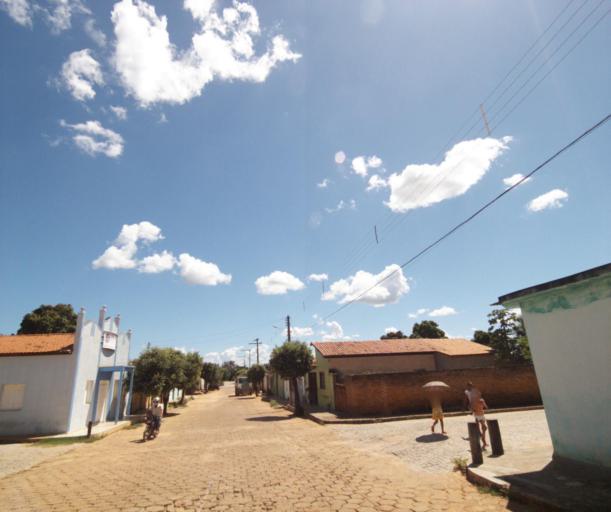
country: BR
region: Bahia
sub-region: Carinhanha
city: Carinhanha
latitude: -14.2128
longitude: -44.2831
